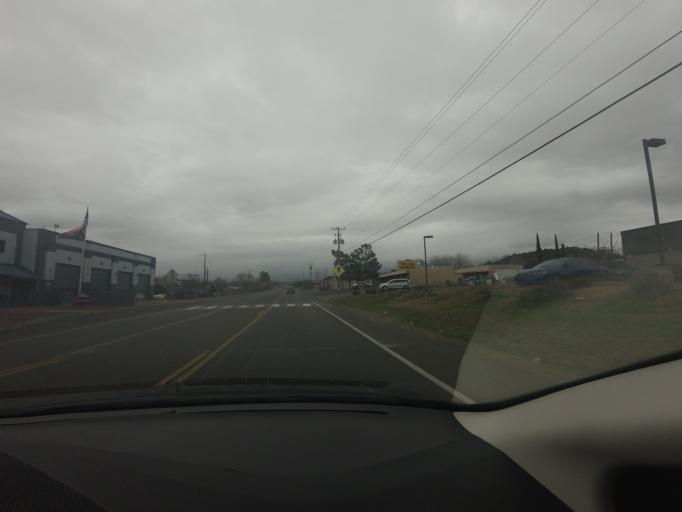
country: US
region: Arizona
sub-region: Yavapai County
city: Lake Montezuma
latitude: 34.6420
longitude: -111.7944
